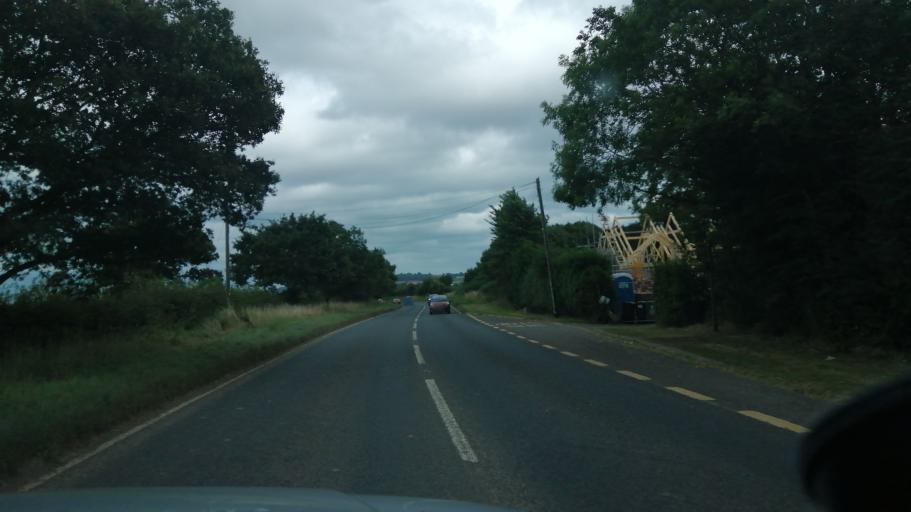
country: GB
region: England
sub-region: Herefordshire
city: Thruxton
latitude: 51.9882
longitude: -2.7956
